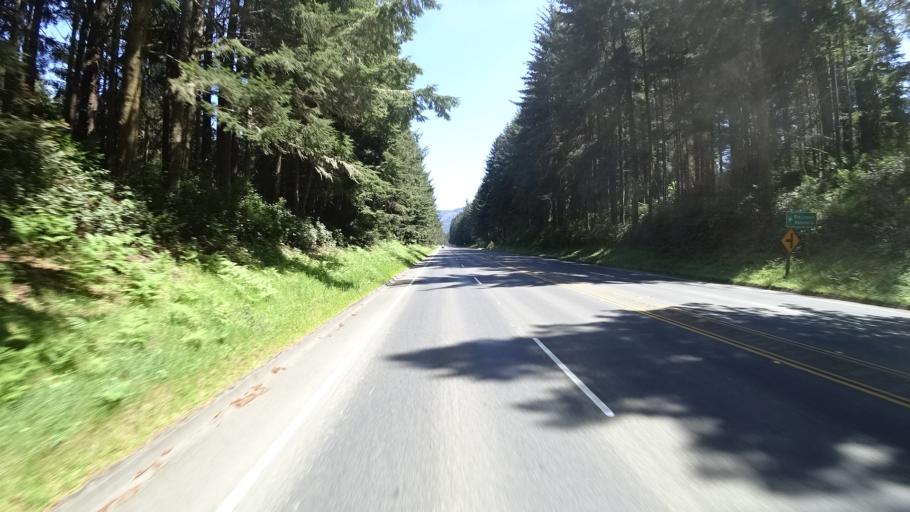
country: US
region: California
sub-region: Humboldt County
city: Westhaven-Moonstone
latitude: 41.1539
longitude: -124.1307
